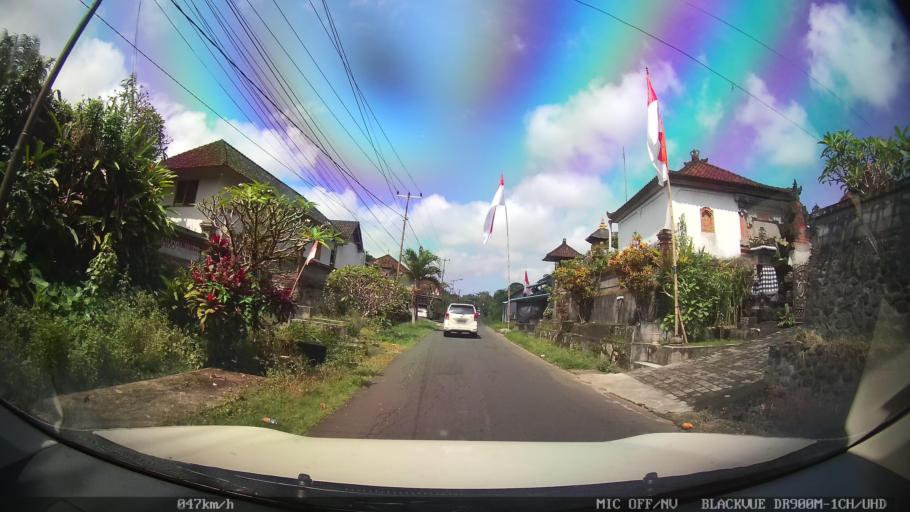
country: ID
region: Bali
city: Banjar Mulung
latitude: -8.5142
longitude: 115.3234
